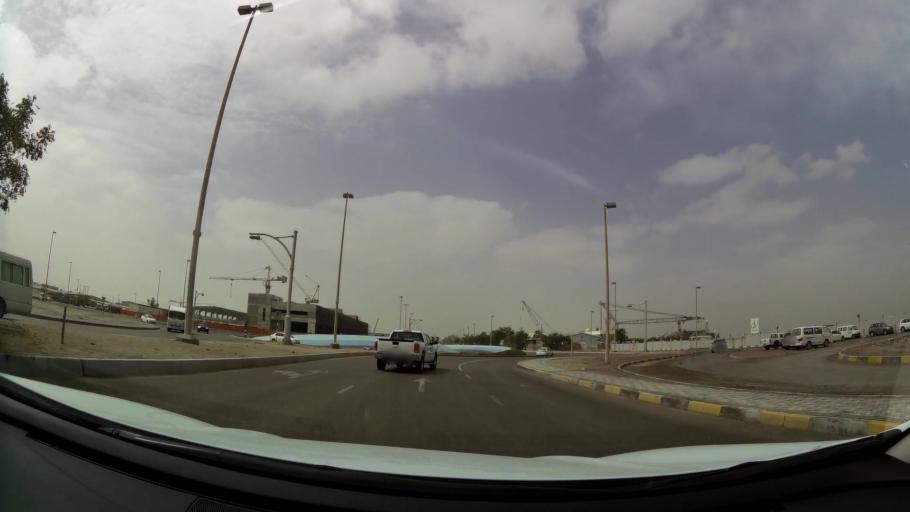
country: AE
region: Abu Dhabi
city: Abu Dhabi
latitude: 24.3812
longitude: 54.4816
